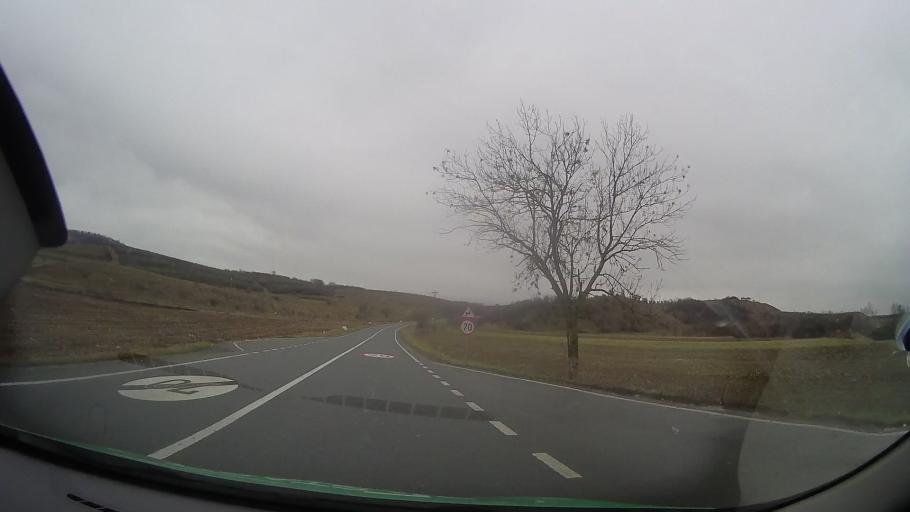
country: RO
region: Mures
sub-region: Comuna Breaza
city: Breaza
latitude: 46.7877
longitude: 24.6457
